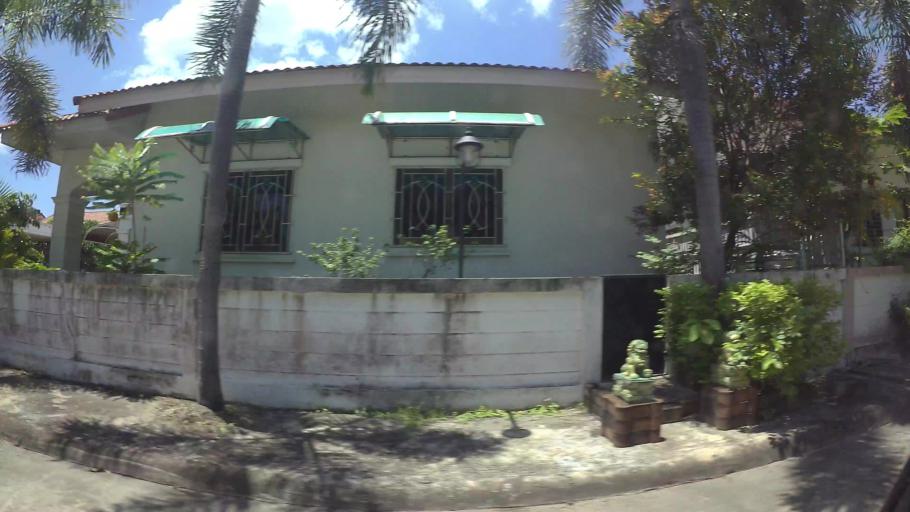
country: TH
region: Chon Buri
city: Si Racha
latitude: 13.1294
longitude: 100.9463
